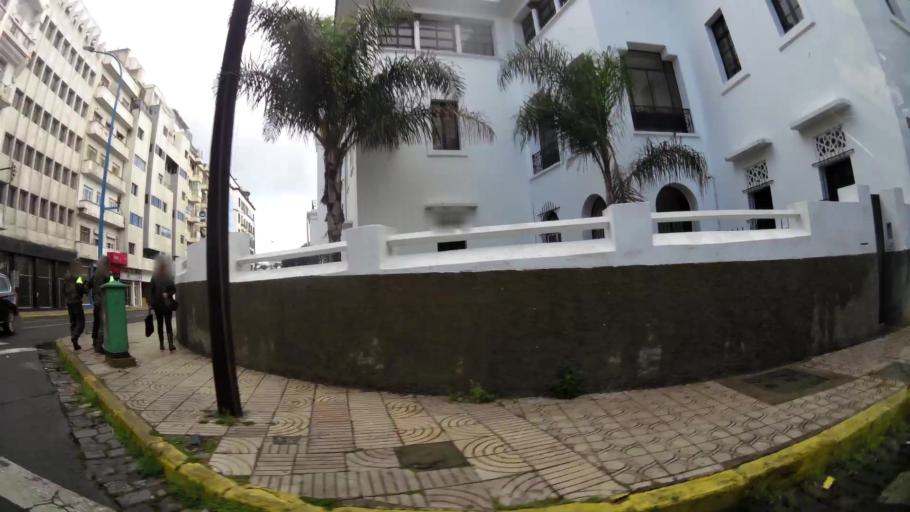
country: MA
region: Grand Casablanca
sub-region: Casablanca
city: Casablanca
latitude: 33.5891
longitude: -7.6184
